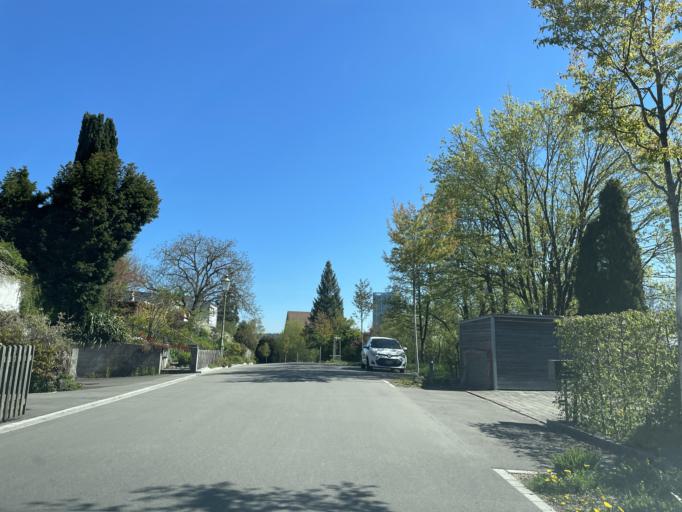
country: CH
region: Zurich
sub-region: Bezirk Winterthur
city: Stadt Winterthur (Kreis 1) / Bruehlberg
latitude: 47.4974
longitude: 8.7112
